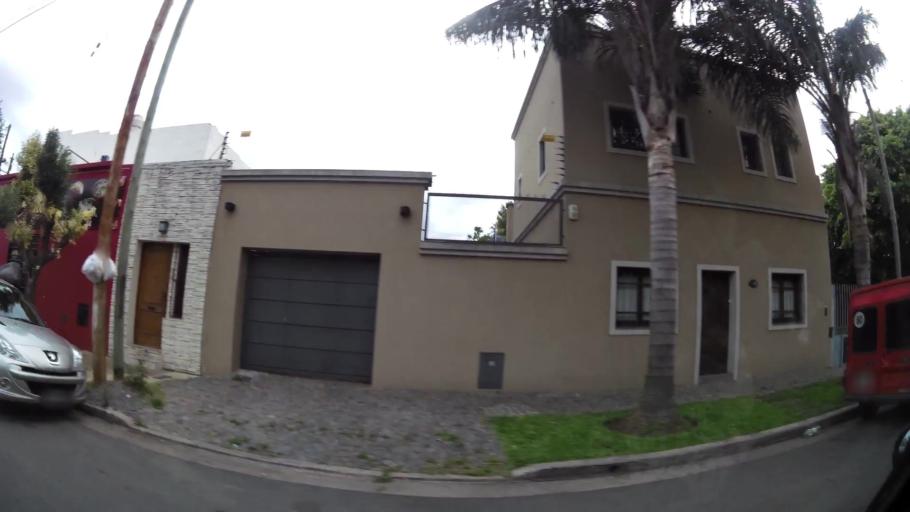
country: AR
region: Buenos Aires
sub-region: Partido de Quilmes
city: Quilmes
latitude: -34.7354
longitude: -58.2471
